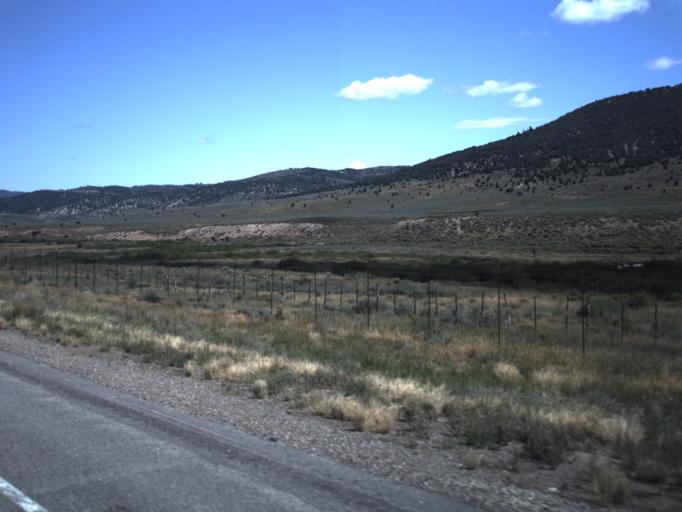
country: US
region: Utah
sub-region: Carbon County
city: Helper
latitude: 39.8987
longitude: -111.0554
